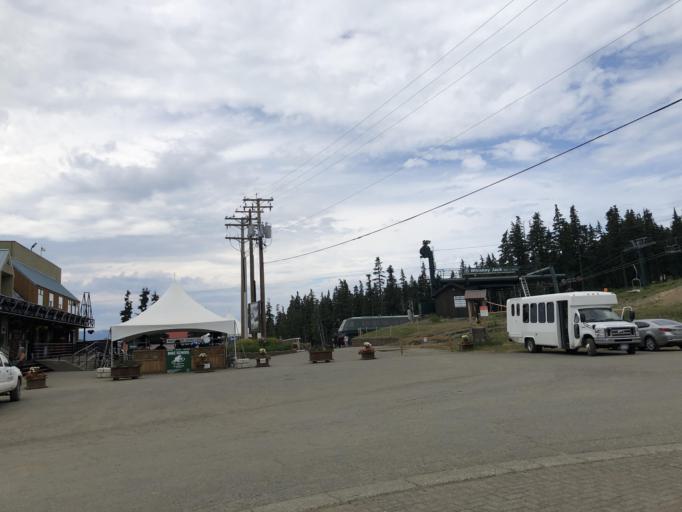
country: CA
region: British Columbia
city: Campbell River
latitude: 49.7413
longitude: -125.3026
